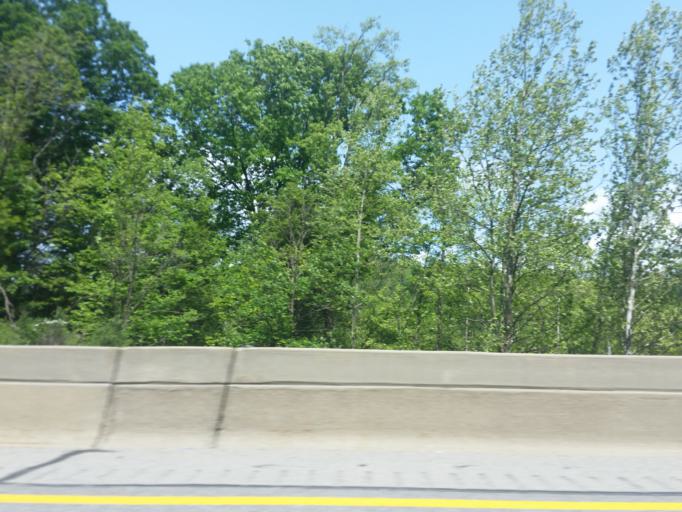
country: US
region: West Virginia
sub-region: Fayette County
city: Oak Hill
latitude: 37.9781
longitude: -81.2957
